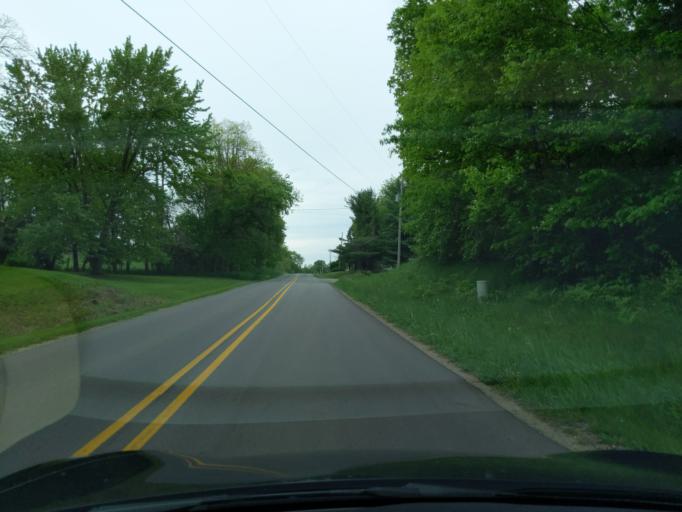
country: US
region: Michigan
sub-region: Jackson County
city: Jackson
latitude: 42.3503
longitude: -84.3487
